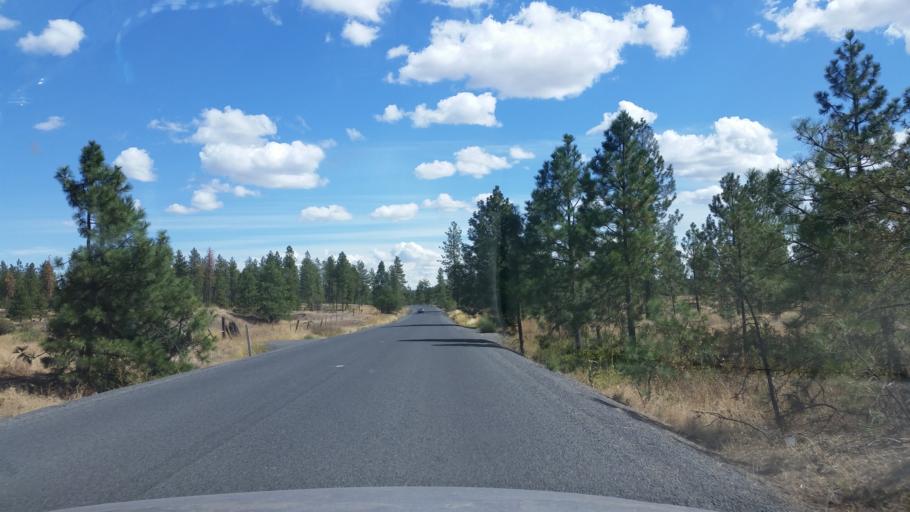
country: US
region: Washington
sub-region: Spokane County
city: Medical Lake
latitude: 47.5036
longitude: -117.6849
